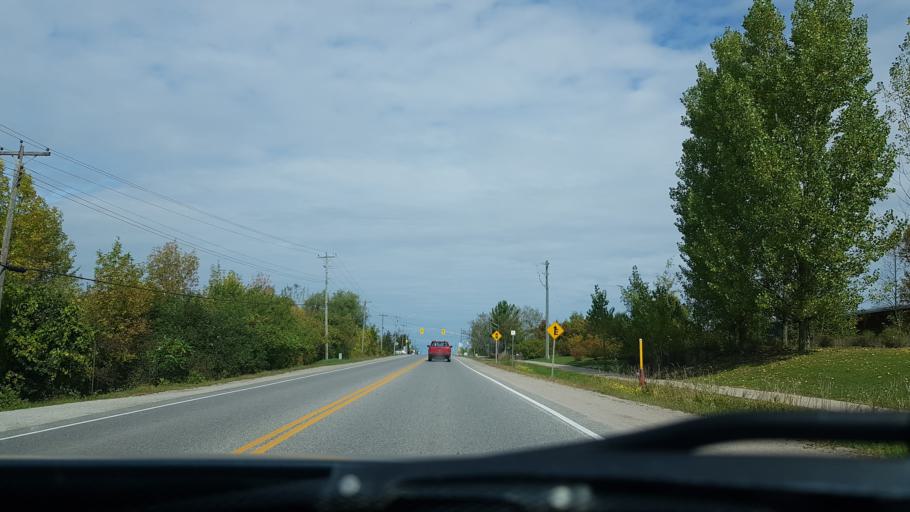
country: CA
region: Ontario
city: Orillia
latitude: 44.6524
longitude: -79.3493
